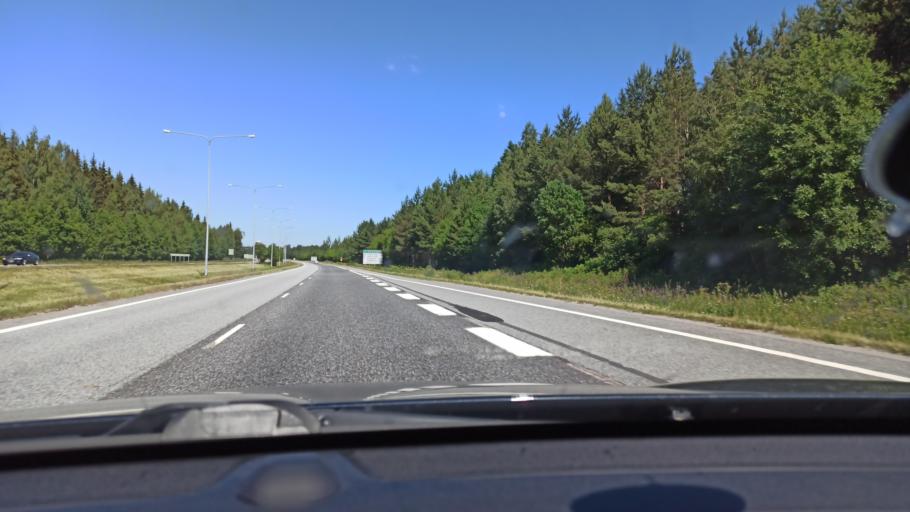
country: FI
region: Ostrobothnia
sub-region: Vaasa
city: Ristinummi
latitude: 63.0590
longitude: 21.7109
